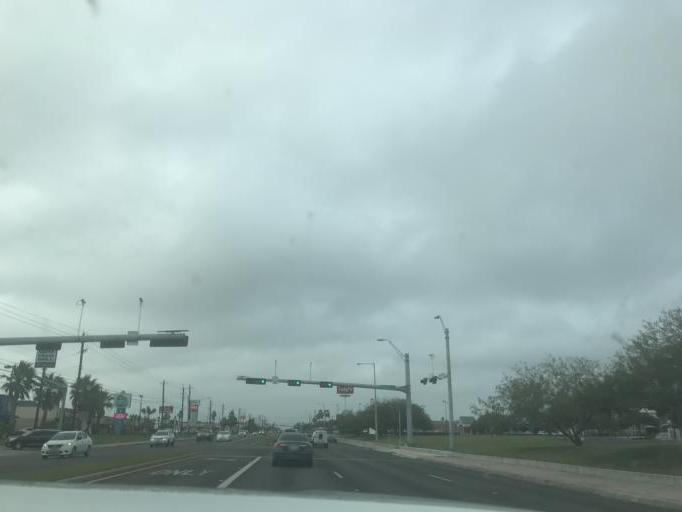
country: US
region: Texas
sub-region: Nueces County
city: Corpus Christi
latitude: 27.6830
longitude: -97.3787
